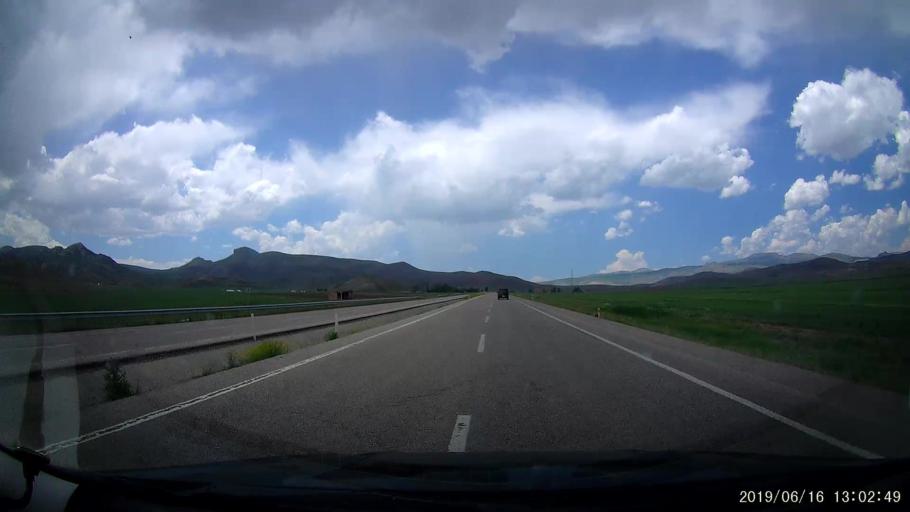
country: TR
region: Agri
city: Sulucem
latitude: 39.5769
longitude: 43.8057
